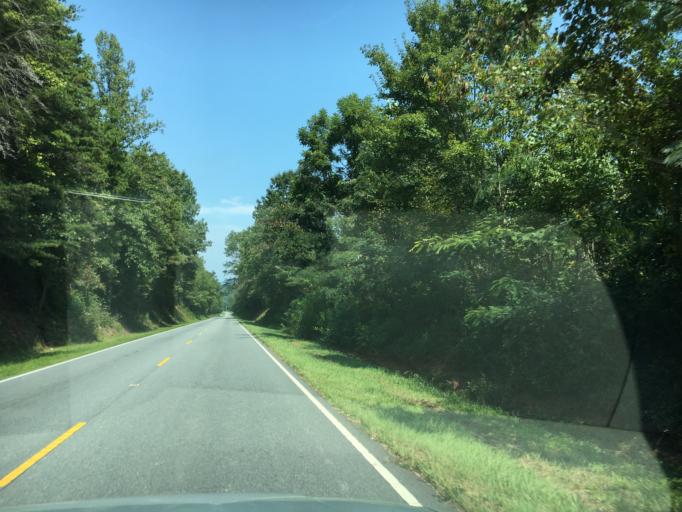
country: US
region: North Carolina
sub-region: Rutherford County
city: Rutherfordton
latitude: 35.5019
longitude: -81.9768
